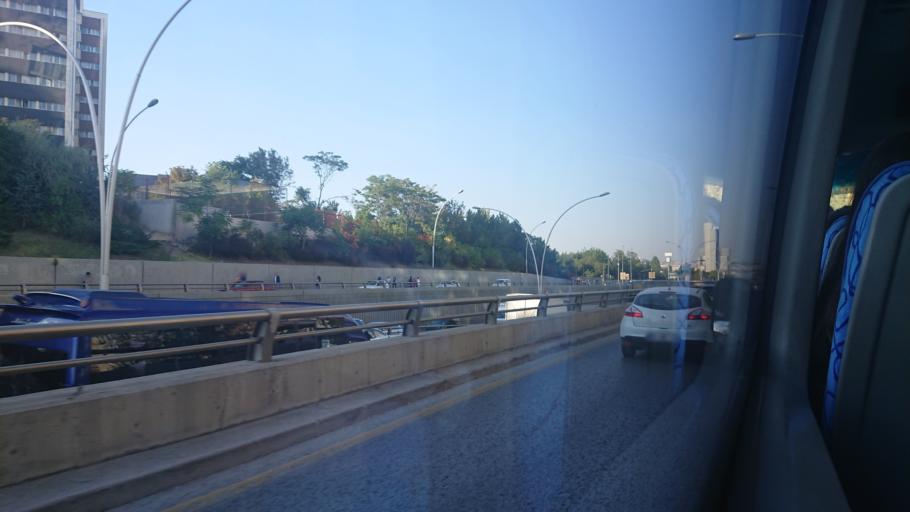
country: TR
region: Ankara
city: Ankara
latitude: 39.9290
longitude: 32.8174
